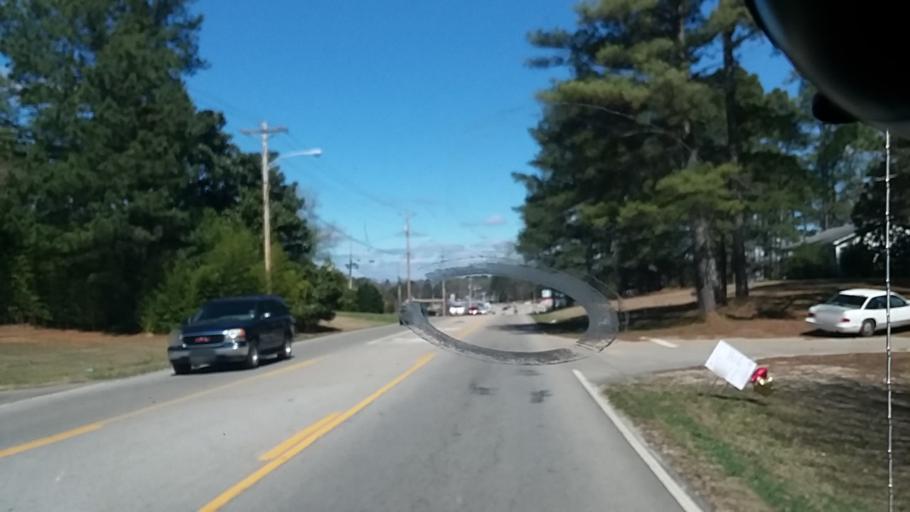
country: US
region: Mississippi
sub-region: Tishomingo County
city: Iuka
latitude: 34.8058
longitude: -88.2016
